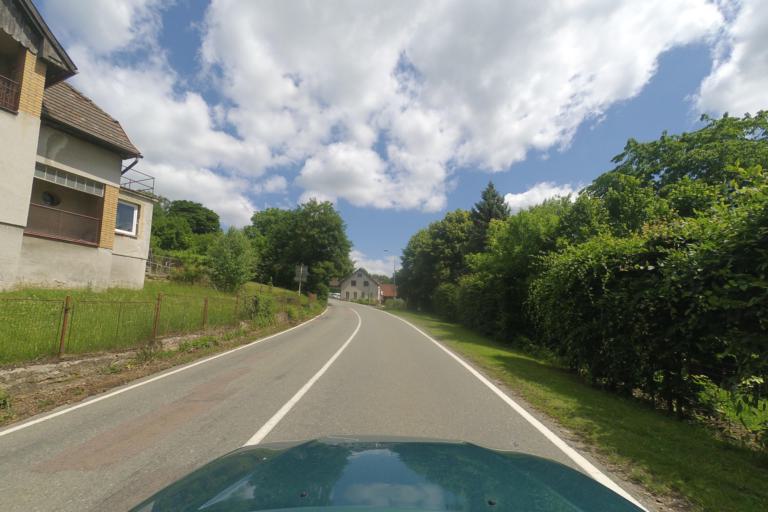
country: CZ
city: Dobruska
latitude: 50.3259
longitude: 16.2136
